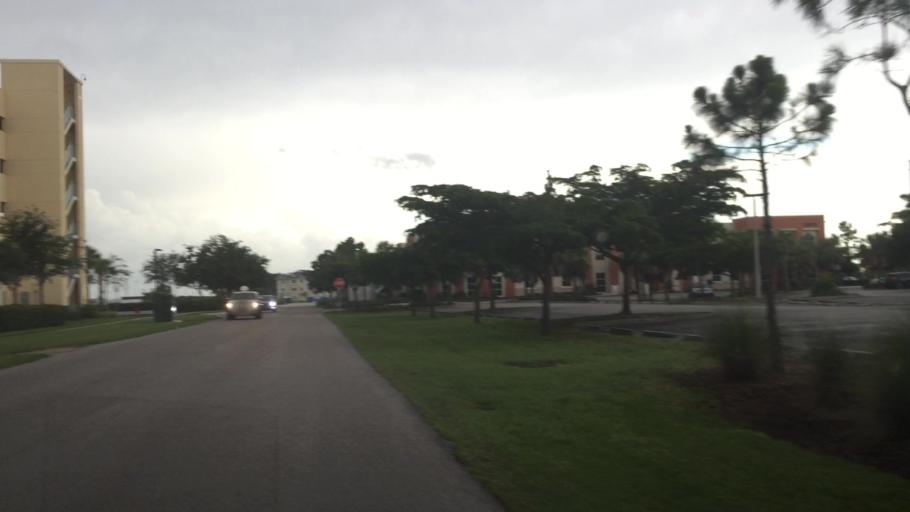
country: US
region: Florida
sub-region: Lee County
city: Villas
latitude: 26.5436
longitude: -81.8513
